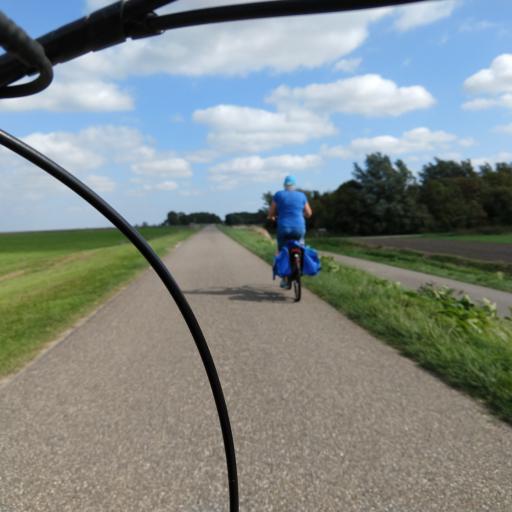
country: NL
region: Zeeland
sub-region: Gemeente Noord-Beveland
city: Kamperland
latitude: 51.5911
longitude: 3.7676
